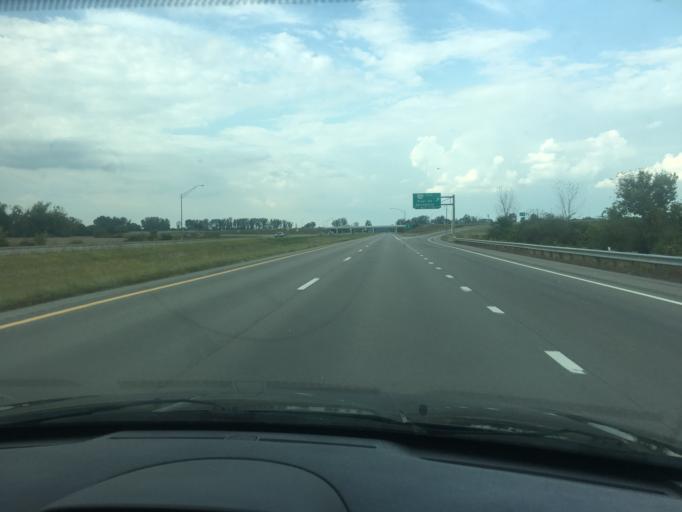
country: US
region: Ohio
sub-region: Clark County
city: Northridge
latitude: 39.9827
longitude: -83.8141
